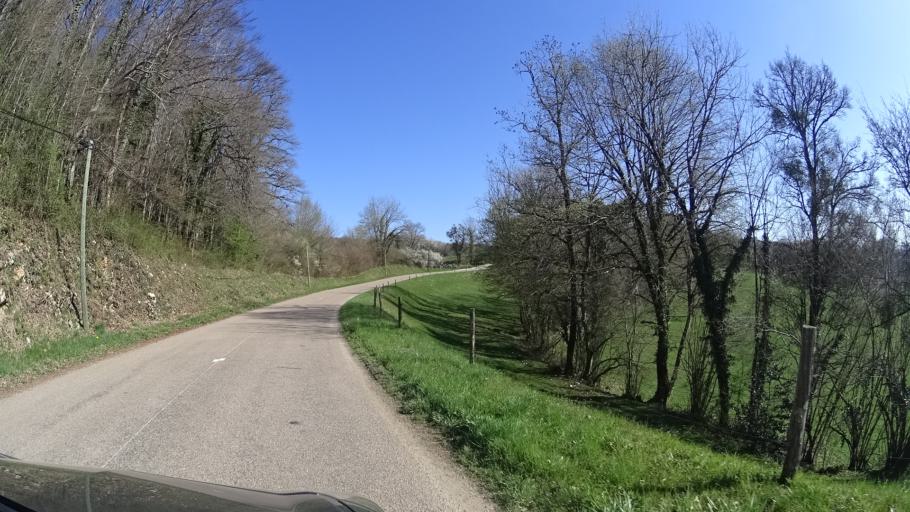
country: FR
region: Franche-Comte
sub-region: Departement du Doubs
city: Ornans
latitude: 47.1226
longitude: 6.0865
